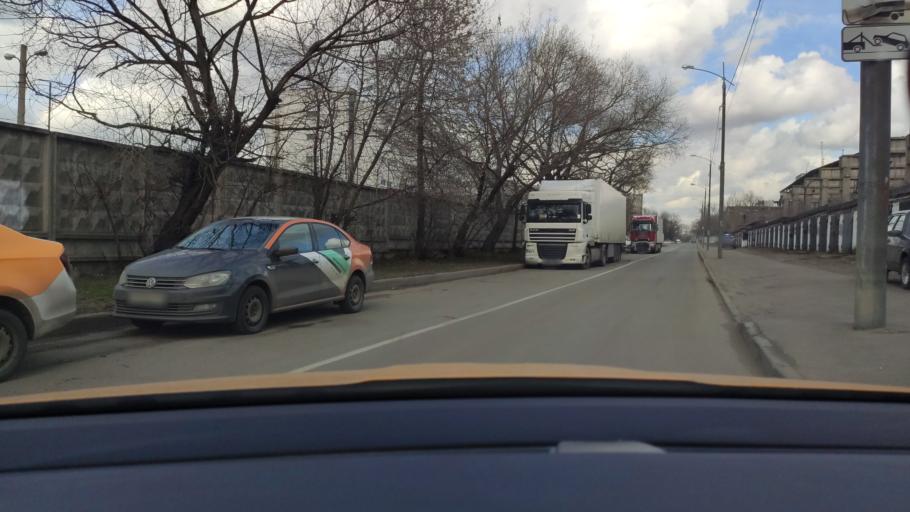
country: RU
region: Moscow
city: Ryazanskiy
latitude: 55.7176
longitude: 37.7638
